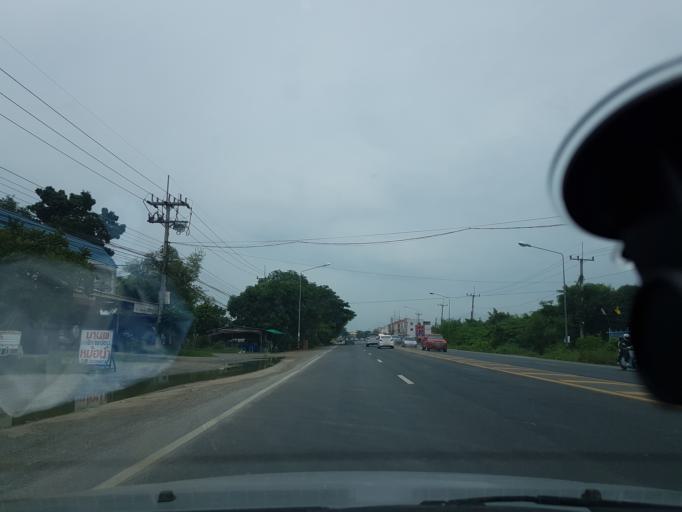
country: TH
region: Lop Buri
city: Lop Buri
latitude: 14.8098
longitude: 100.5960
